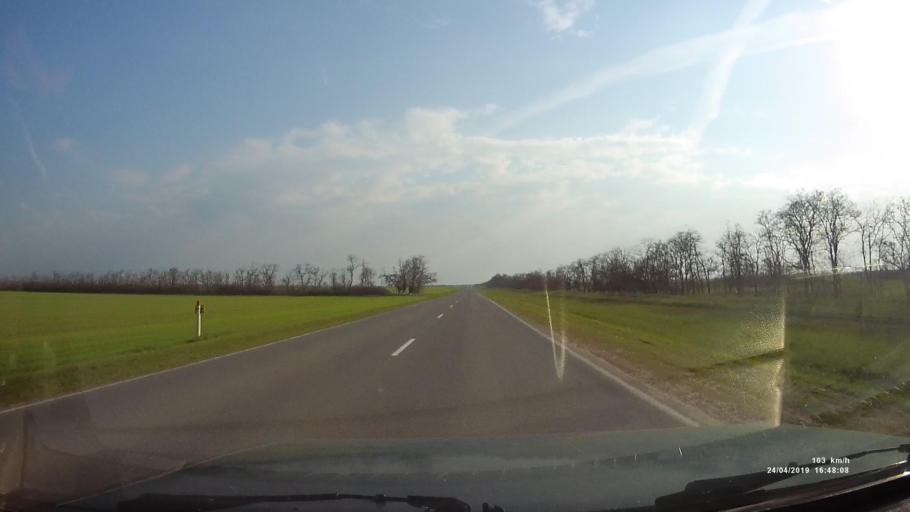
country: RU
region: Rostov
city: Proletarsk
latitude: 46.7352
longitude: 41.7786
